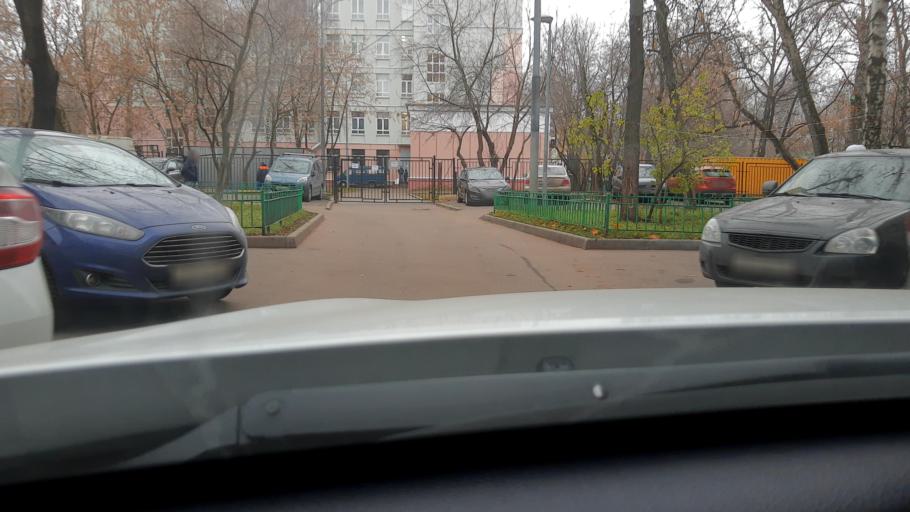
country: RU
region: Moscow
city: Novyye Kuz'minki
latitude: 55.7099
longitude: 37.7607
